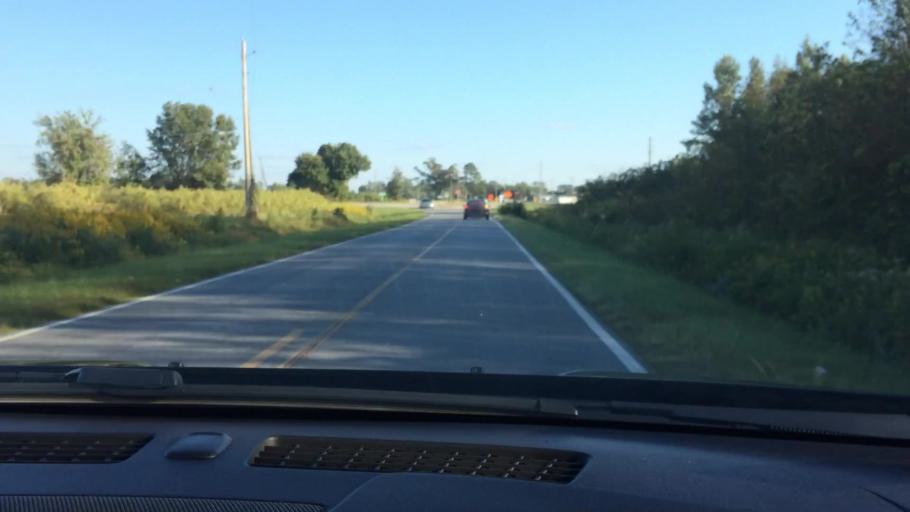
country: US
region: North Carolina
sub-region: Pitt County
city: Ayden
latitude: 35.4930
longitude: -77.4299
